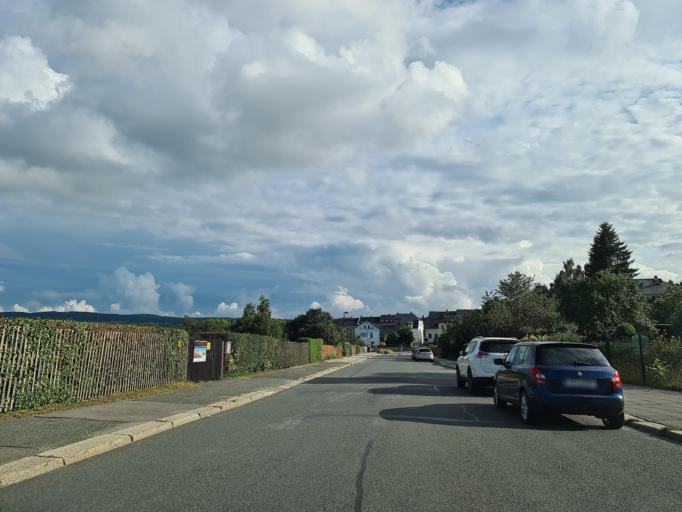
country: DE
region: Saxony
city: Auerbach
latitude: 50.5106
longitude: 12.3892
